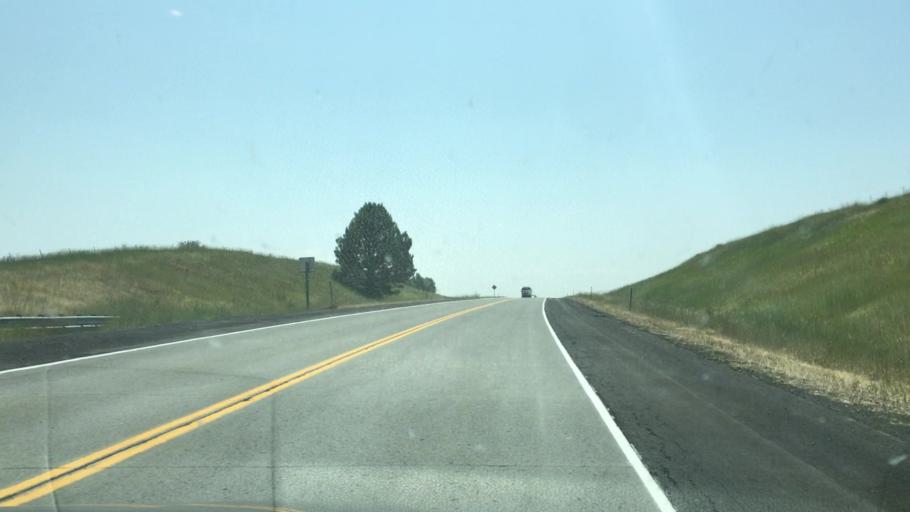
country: US
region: Idaho
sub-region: Lewis County
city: Nezperce
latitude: 46.0960
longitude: -116.3494
